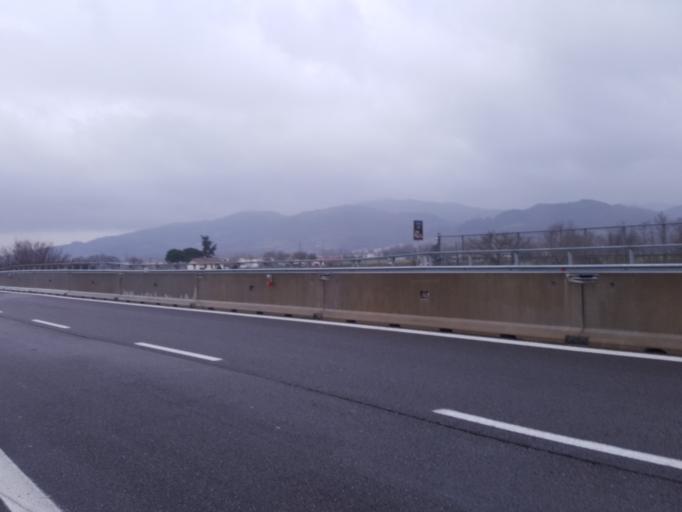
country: IT
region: Umbria
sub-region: Provincia di Perugia
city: Cerbara
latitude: 43.5000
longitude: 12.1966
